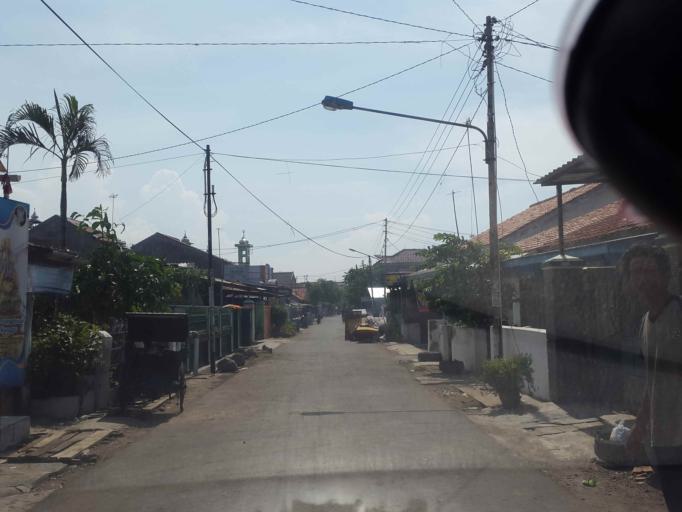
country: ID
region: Central Java
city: Tegal
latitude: -6.8544
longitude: 109.1324
